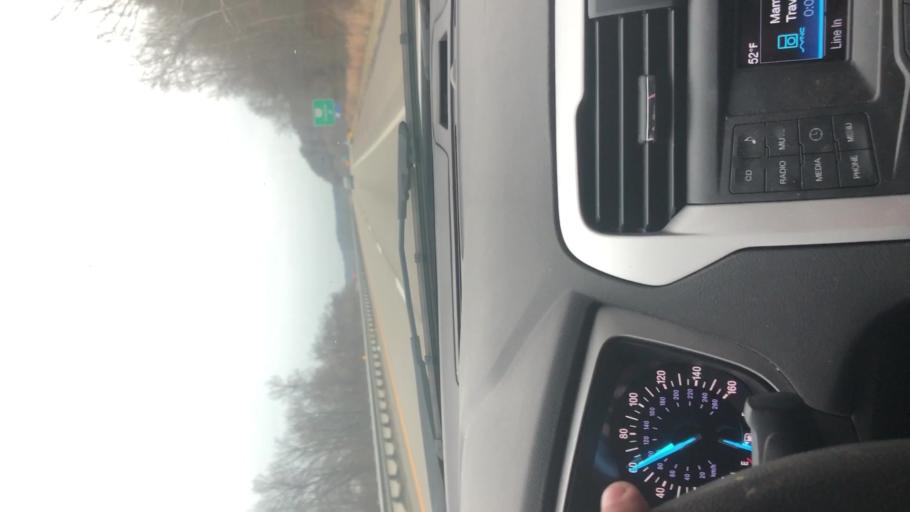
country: US
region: Ohio
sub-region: Lawrence County
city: Coal Grove
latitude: 38.5218
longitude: -82.6600
